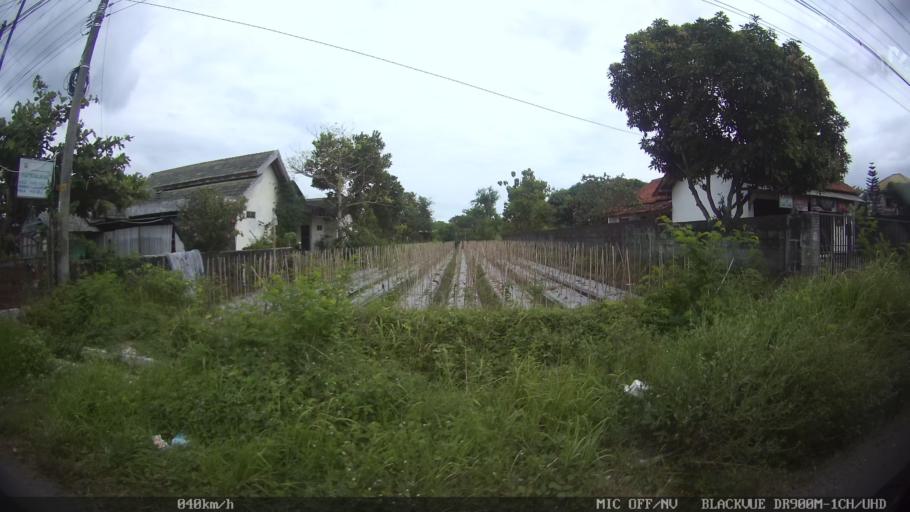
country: ID
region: Daerah Istimewa Yogyakarta
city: Depok
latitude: -7.8241
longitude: 110.4425
